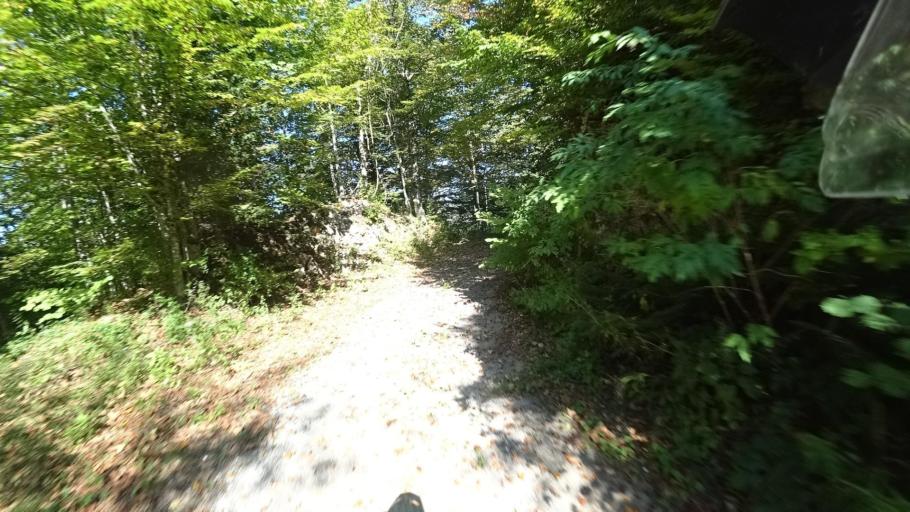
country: HR
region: Karlovacka
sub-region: Grad Ogulin
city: Ogulin
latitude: 45.1758
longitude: 15.1431
